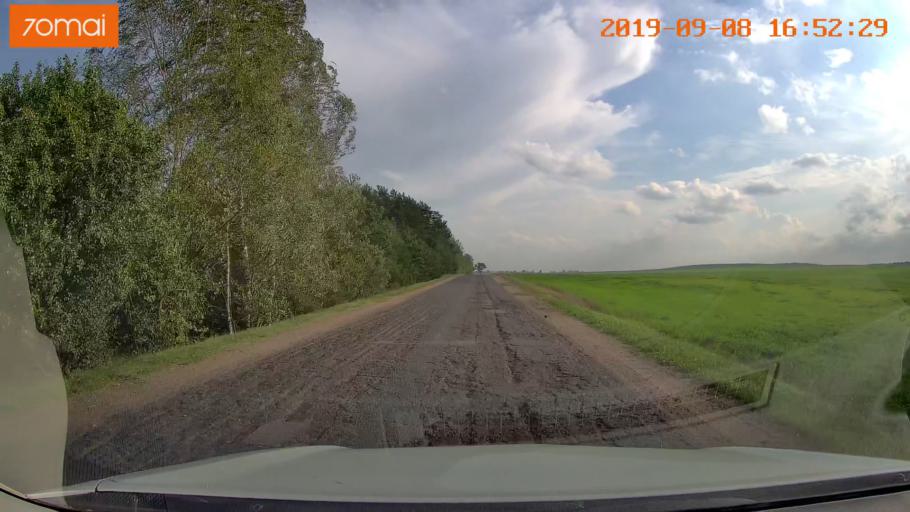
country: BY
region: Grodnenskaya
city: Hrodna
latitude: 53.7738
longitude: 23.9040
